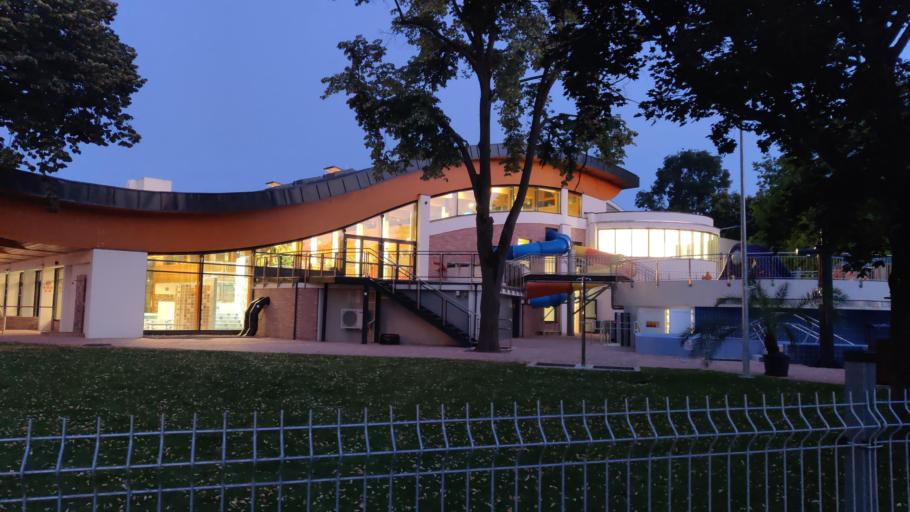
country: HU
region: Baranya
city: Harkany
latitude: 45.8518
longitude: 18.2375
